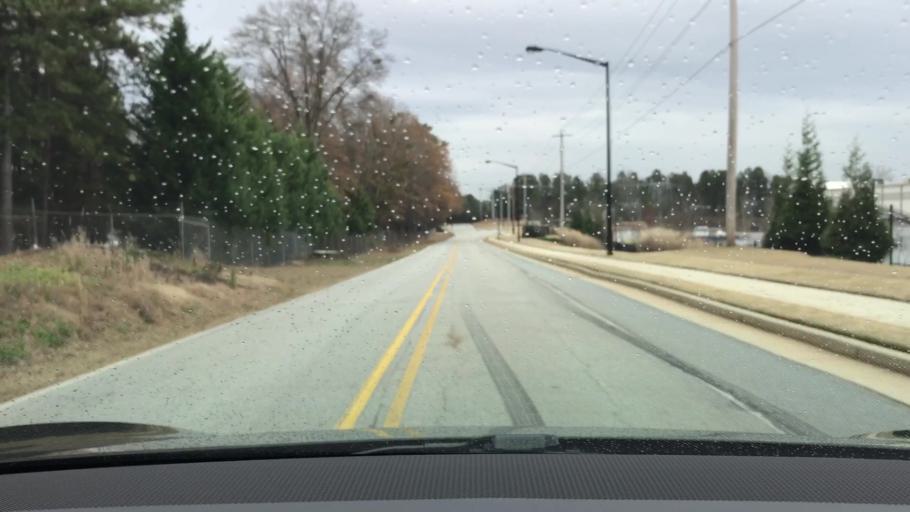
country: US
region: Georgia
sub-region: Gwinnett County
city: Buford
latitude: 34.1101
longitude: -84.0096
